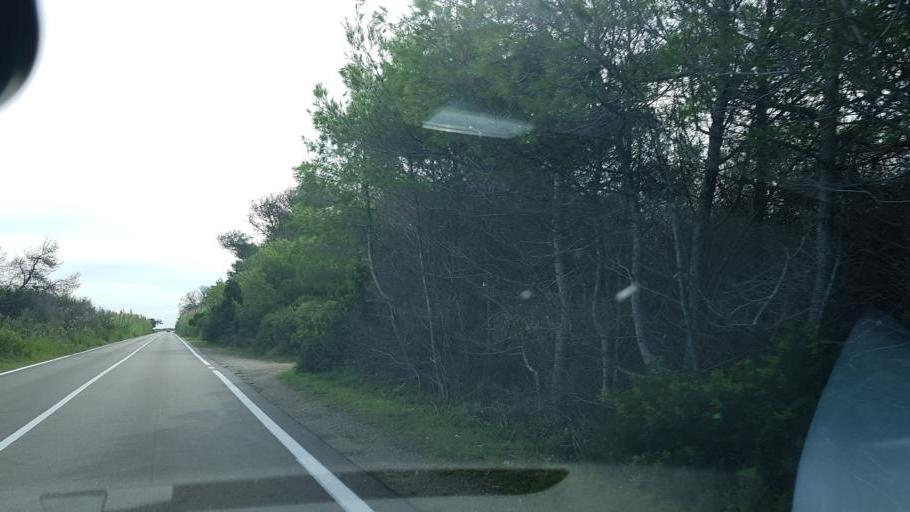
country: IT
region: Apulia
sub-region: Provincia di Lecce
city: Melendugno
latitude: 40.3366
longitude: 18.3624
